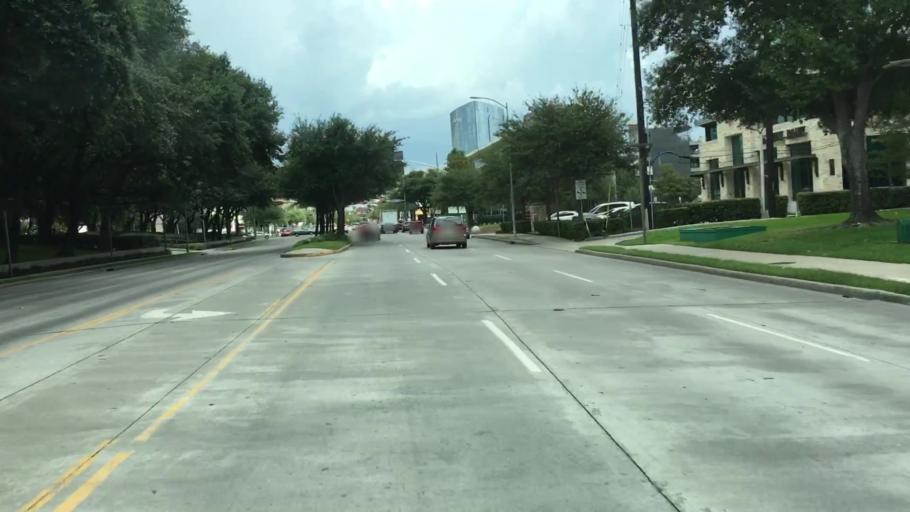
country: US
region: Texas
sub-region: Harris County
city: Hunters Creek Village
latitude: 29.7502
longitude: -95.4648
